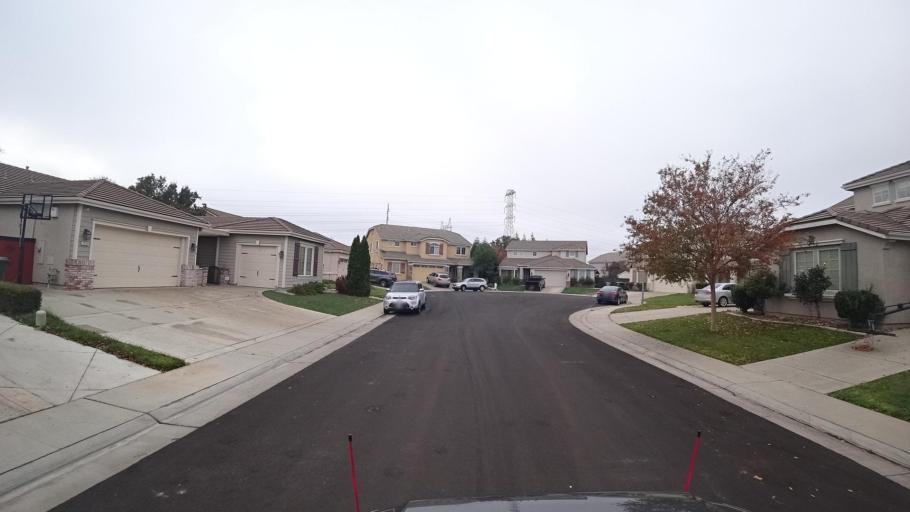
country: US
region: California
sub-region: Sacramento County
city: Elk Grove
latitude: 38.3907
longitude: -121.3493
